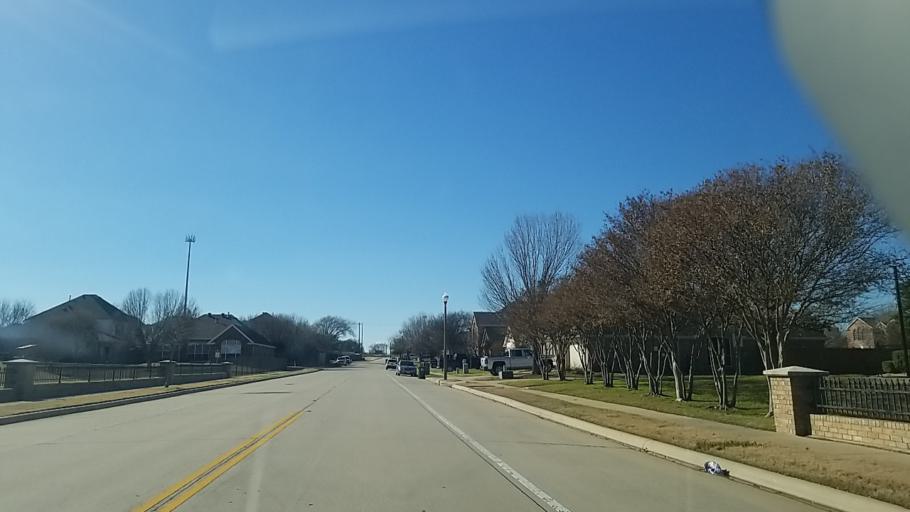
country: US
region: Texas
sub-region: Denton County
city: Corinth
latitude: 33.1513
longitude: -97.0942
